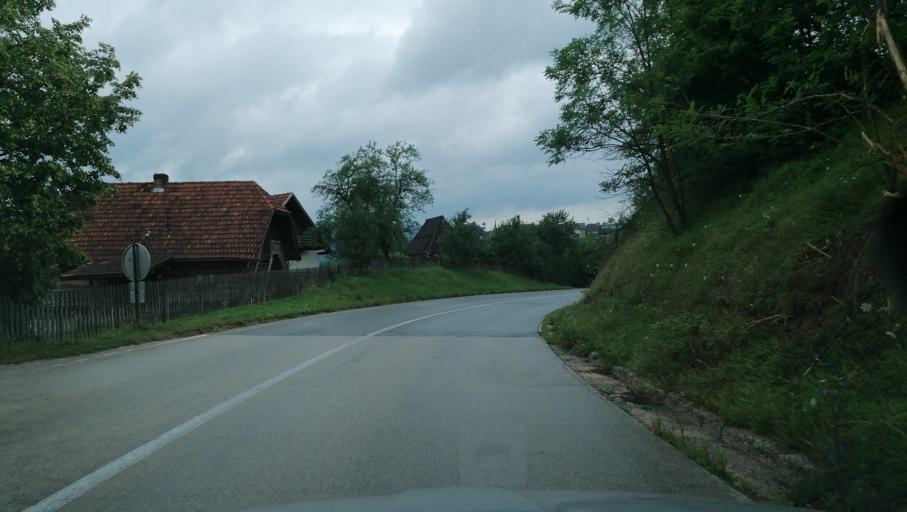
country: RS
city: Durici
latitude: 43.8007
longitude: 19.5102
